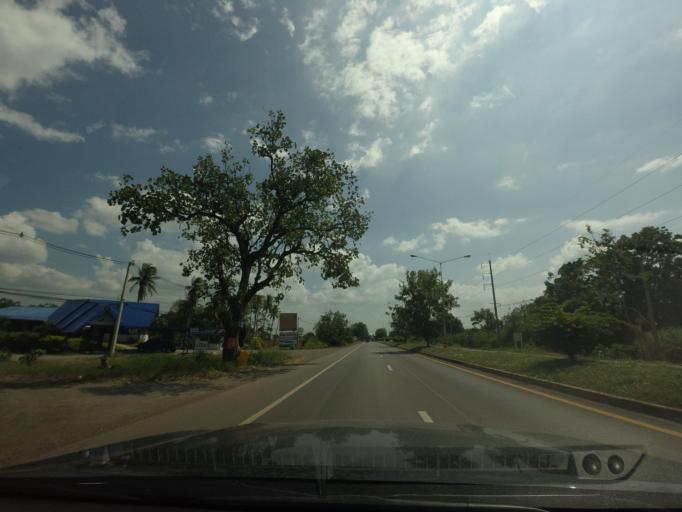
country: TH
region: Phetchabun
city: Nong Phai
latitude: 15.9037
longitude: 101.0275
